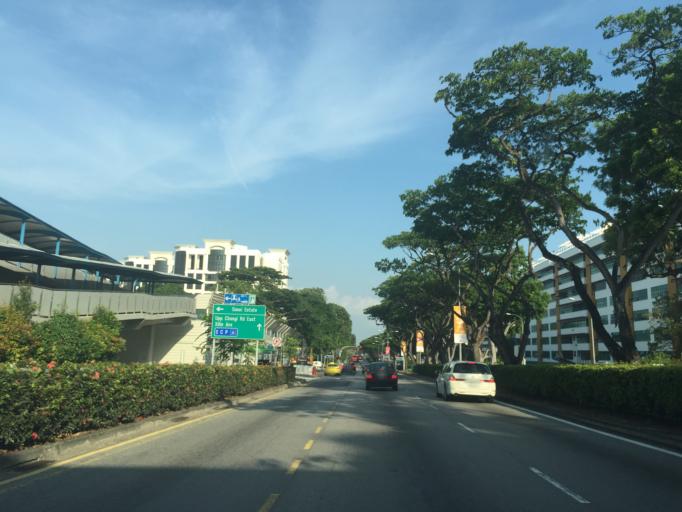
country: SG
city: Singapore
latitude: 1.3397
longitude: 103.9486
